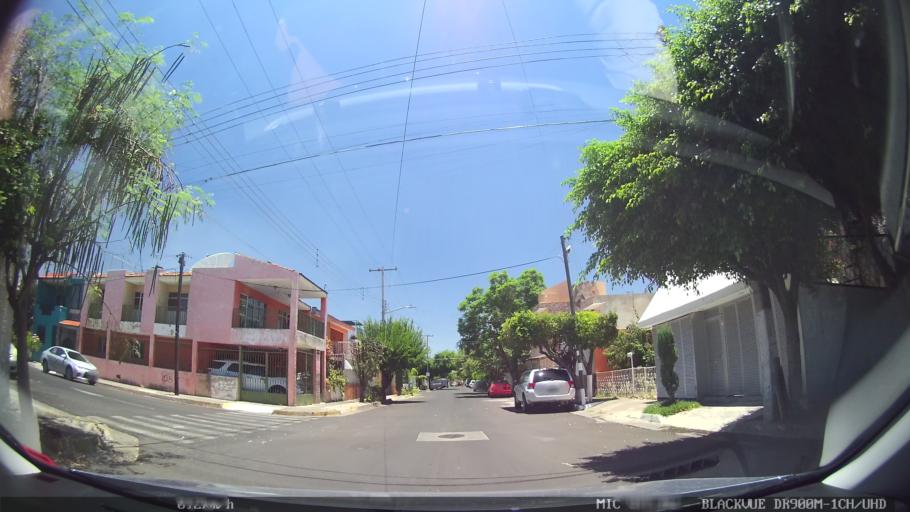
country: MX
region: Jalisco
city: Tlaquepaque
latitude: 20.6783
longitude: -103.2851
